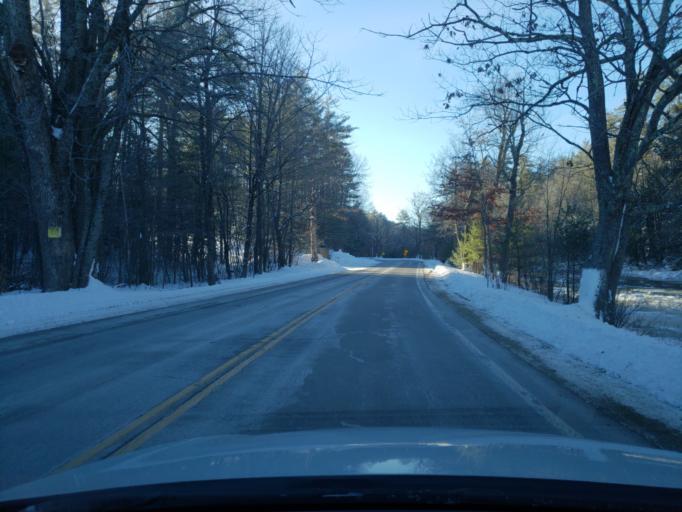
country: US
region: New Hampshire
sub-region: Hillsborough County
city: New Boston
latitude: 42.9970
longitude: -71.6696
